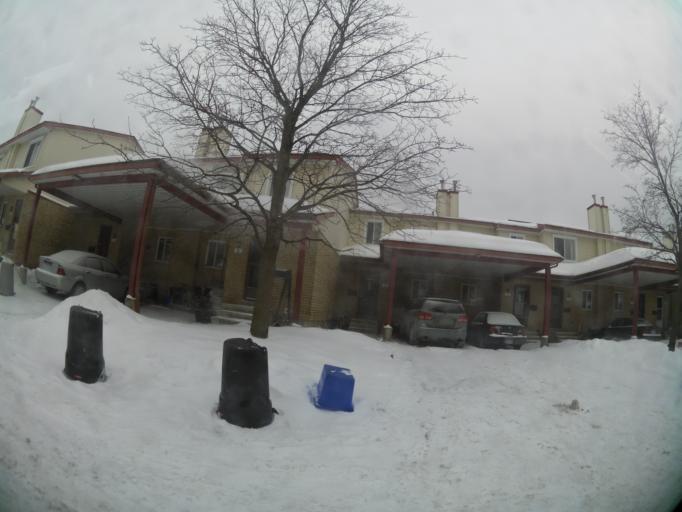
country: CA
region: Ontario
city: Ottawa
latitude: 45.3698
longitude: -75.6095
